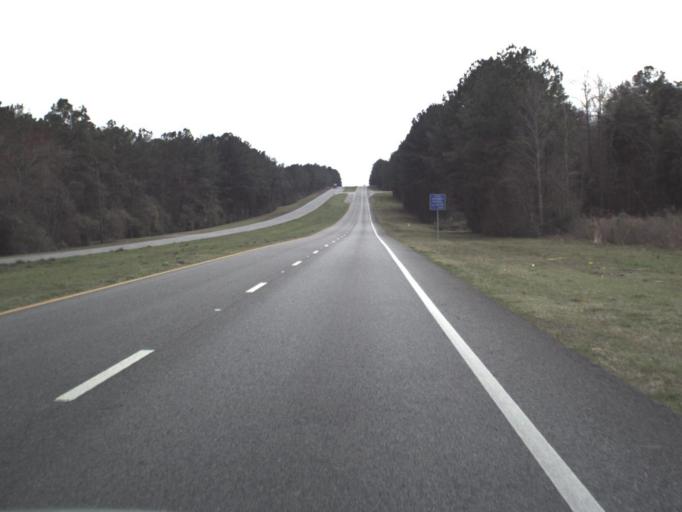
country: US
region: Florida
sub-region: Bay County
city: Youngstown
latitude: 30.5645
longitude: -85.3886
